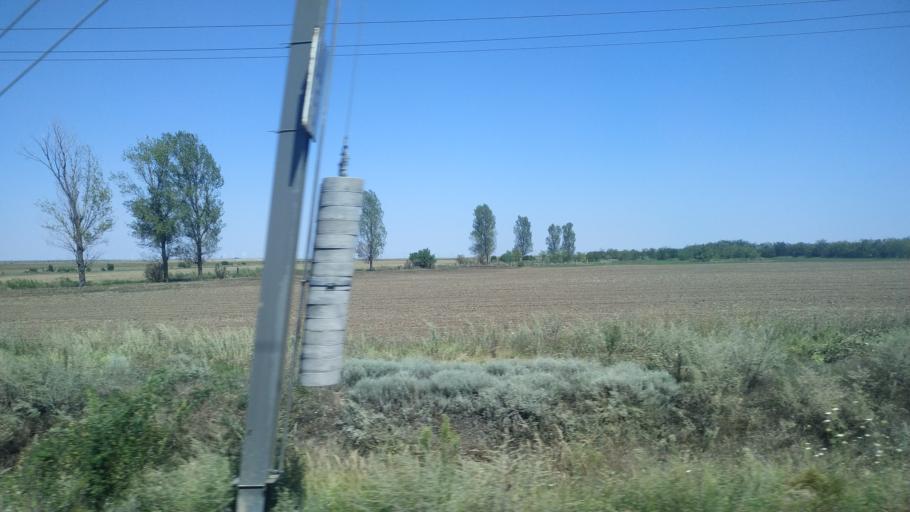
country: RO
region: Ialomita
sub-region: Municipiul Fetesti
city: Fetesti-Gara
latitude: 44.4178
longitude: 27.7945
